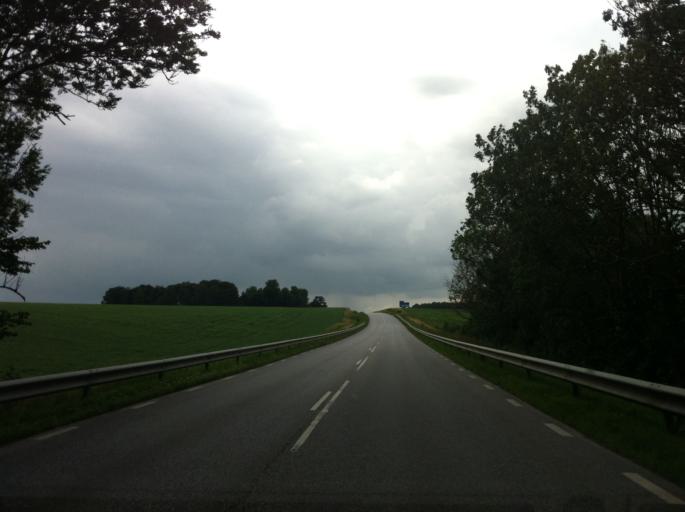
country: SE
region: Skane
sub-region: Eslovs Kommun
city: Eslov
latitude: 55.7659
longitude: 13.3233
